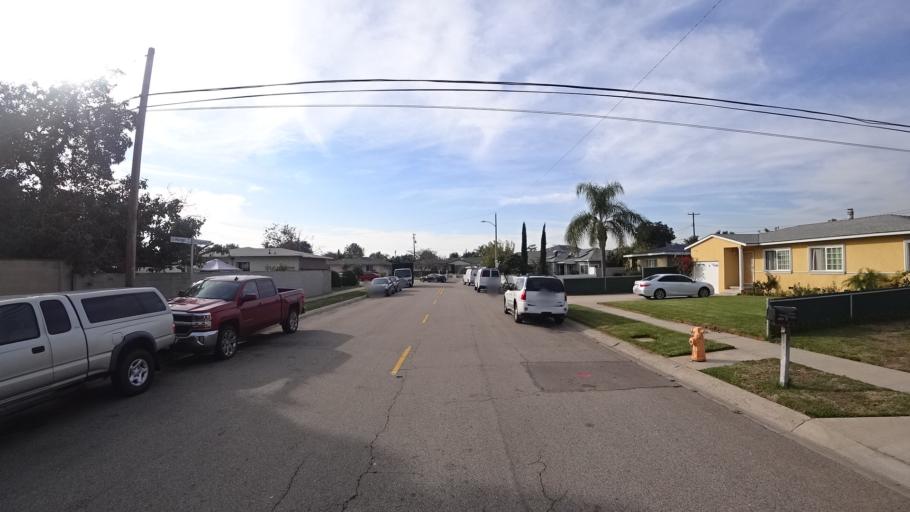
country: US
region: California
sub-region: Orange County
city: Garden Grove
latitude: 33.7630
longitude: -117.9147
